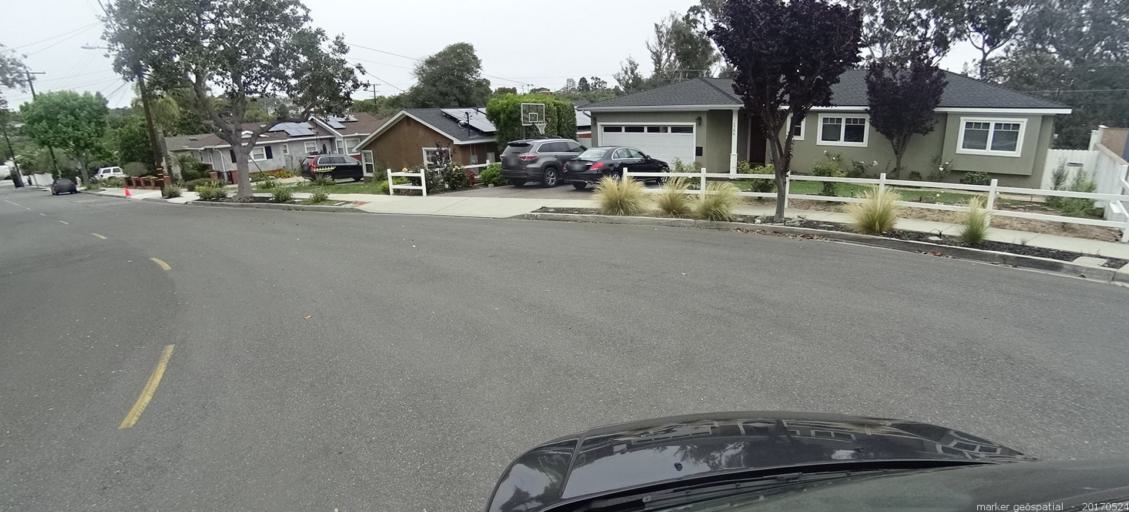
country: US
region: California
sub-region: Los Angeles County
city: Palos Verdes Estates
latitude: 33.8184
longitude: -118.3754
